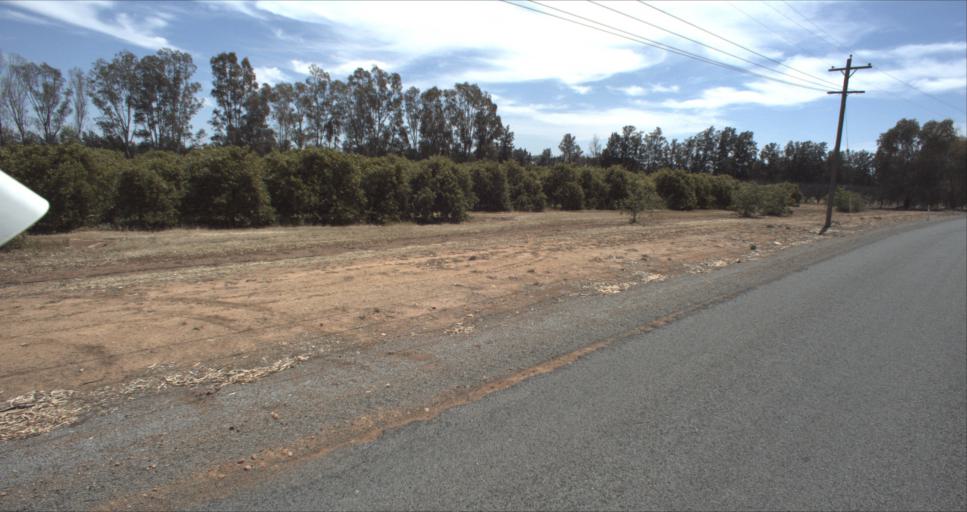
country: AU
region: New South Wales
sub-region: Leeton
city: Leeton
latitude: -34.5737
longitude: 146.4319
